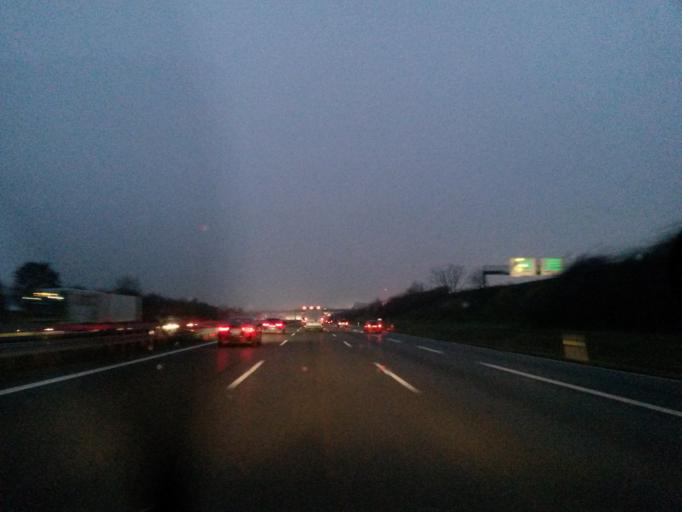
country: DE
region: Baden-Wuerttemberg
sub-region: Regierungsbezirk Stuttgart
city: Leinfelden-Echterdingen
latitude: 48.7009
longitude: 9.1811
